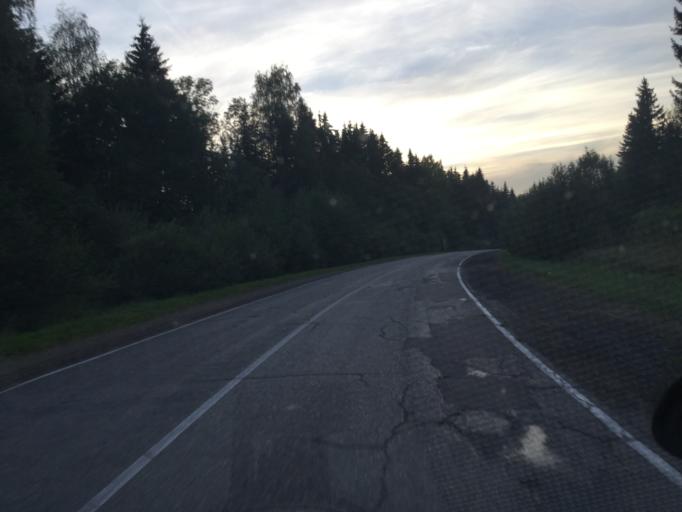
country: RU
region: Pskov
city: Nevel'
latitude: 55.9831
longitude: 30.0052
